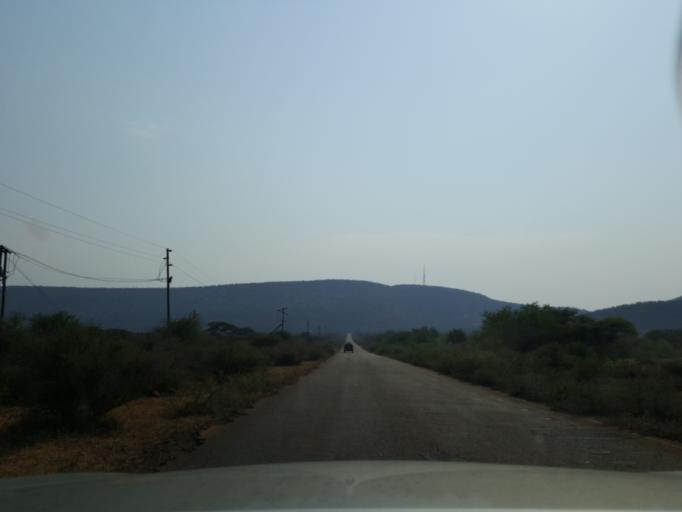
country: BW
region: South East
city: Lobatse
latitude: -25.2930
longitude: 25.8499
